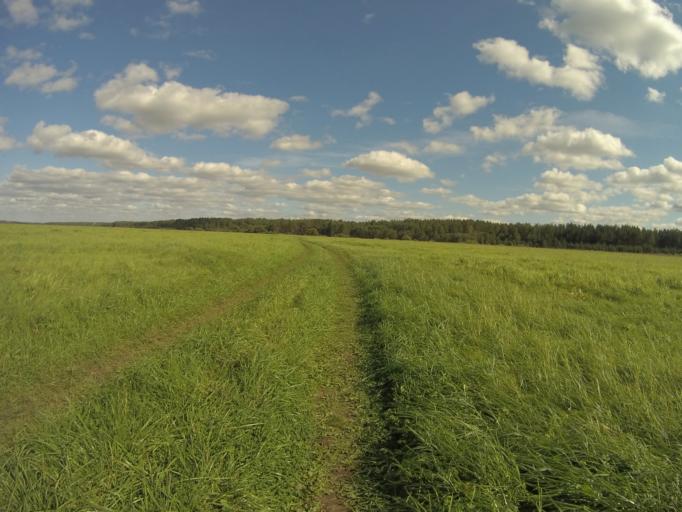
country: RU
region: Vladimir
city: Orgtrud
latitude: 56.3014
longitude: 40.6791
